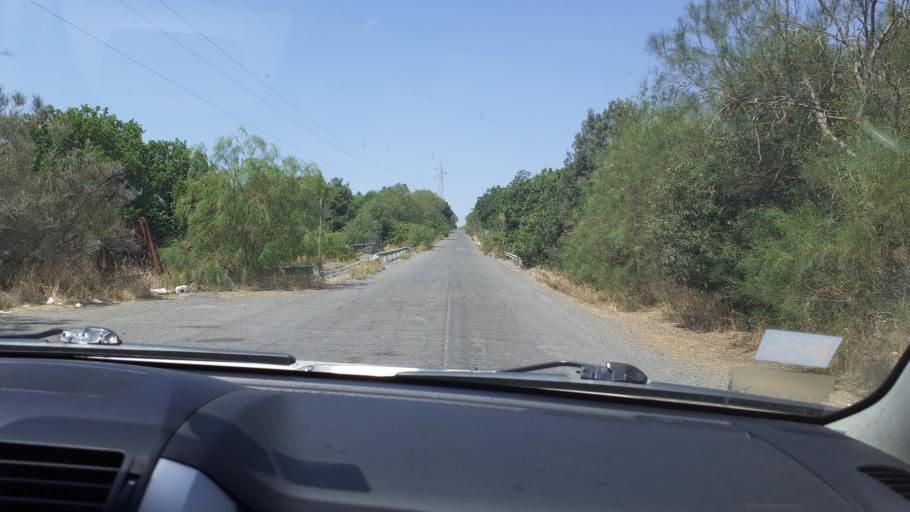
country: IT
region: Sicily
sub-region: Catania
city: Nicolosi
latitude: 37.6475
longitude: 15.0197
